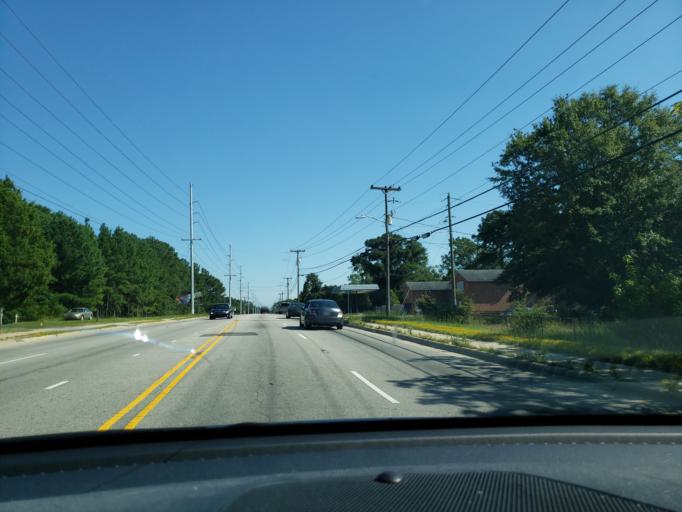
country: US
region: North Carolina
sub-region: Cumberland County
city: Fayetteville
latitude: 35.0947
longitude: -78.9135
